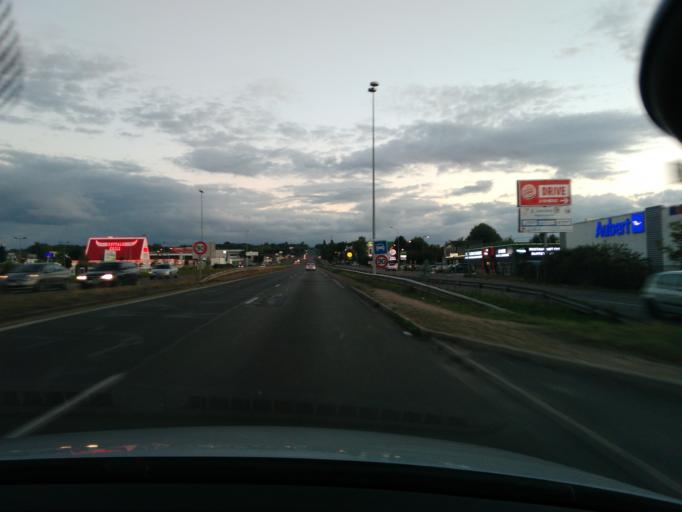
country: FR
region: Ile-de-France
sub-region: Departement de Seine-et-Marne
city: Meaux
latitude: 48.9417
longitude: 2.8794
